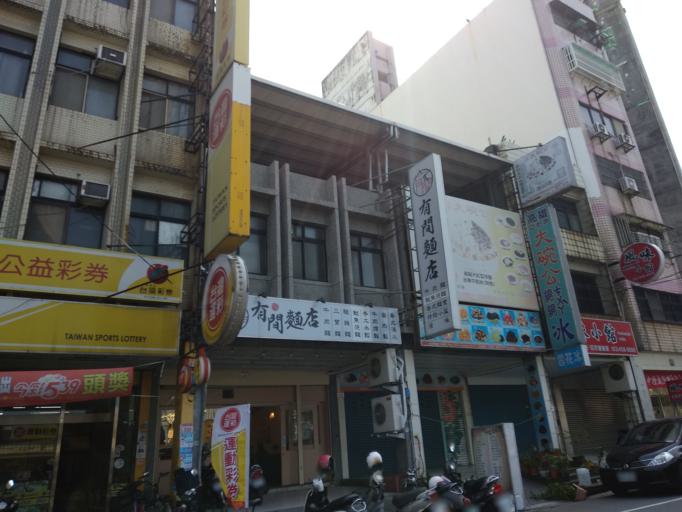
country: TW
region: Taiwan
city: Taoyuan City
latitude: 24.9534
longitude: 121.2302
